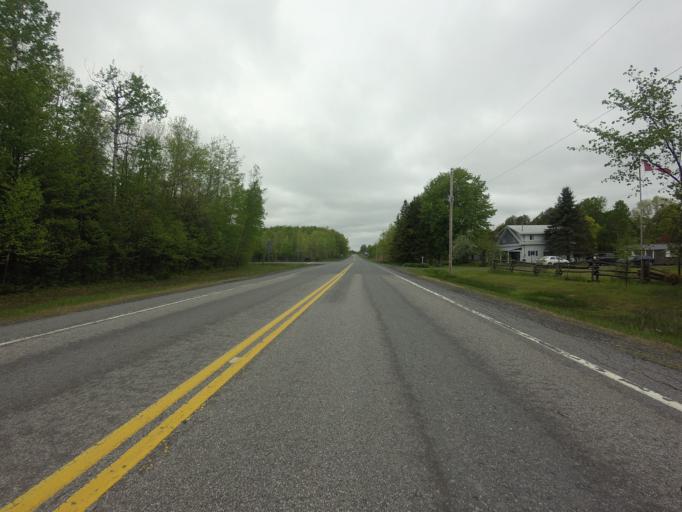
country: US
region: New York
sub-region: St. Lawrence County
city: Norfolk
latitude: 44.9914
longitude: -75.1611
